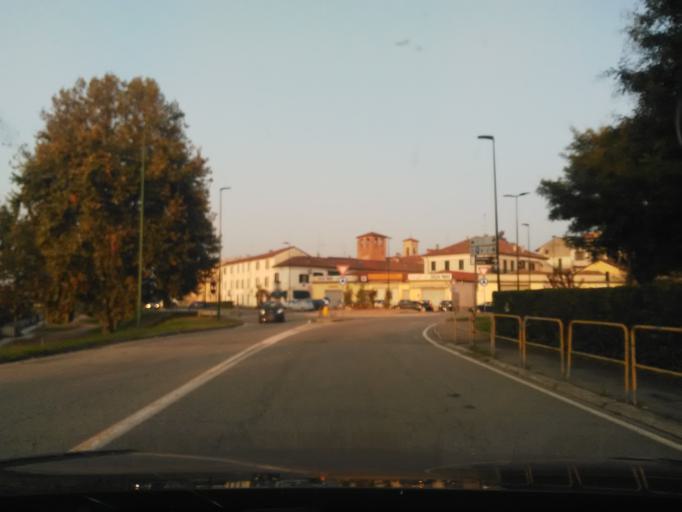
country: IT
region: Piedmont
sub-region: Provincia di Alessandria
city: Casale Monferrato
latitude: 45.1385
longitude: 8.4460
